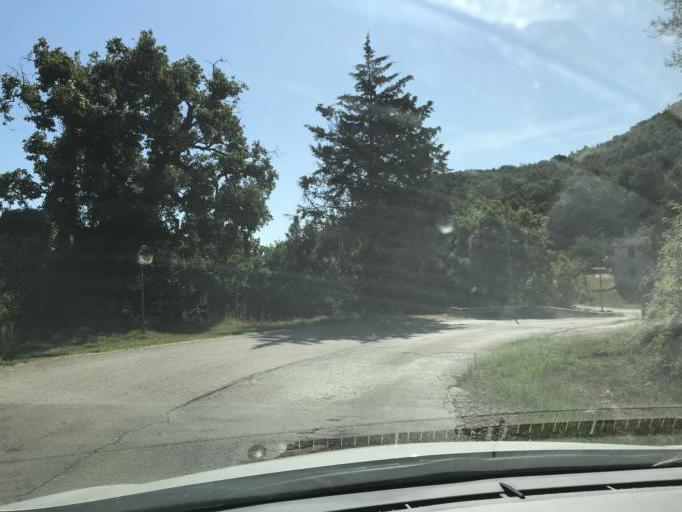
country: IT
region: Umbria
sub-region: Provincia di Terni
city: Avigliano Umbro
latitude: 42.6167
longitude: 12.4052
